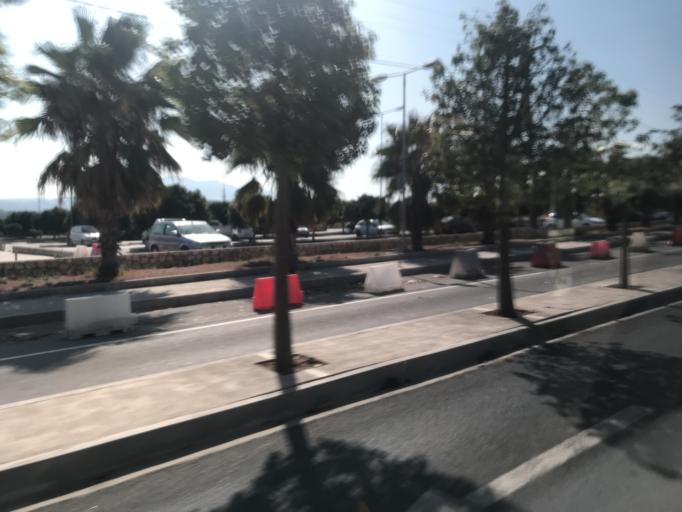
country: GR
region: Crete
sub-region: Nomos Irakleiou
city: Gazi
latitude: 35.3041
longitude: 25.0852
